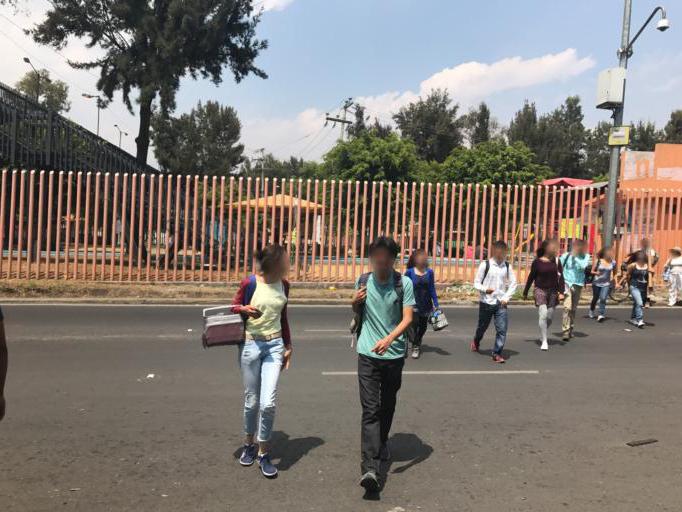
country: MX
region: Mexico City
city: Iztapalapa
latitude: 19.3081
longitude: -99.0838
